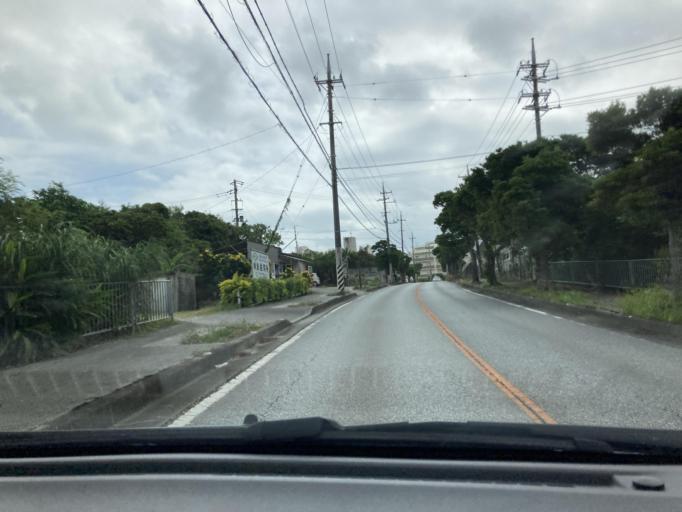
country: JP
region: Okinawa
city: Ginowan
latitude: 26.2587
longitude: 127.7765
